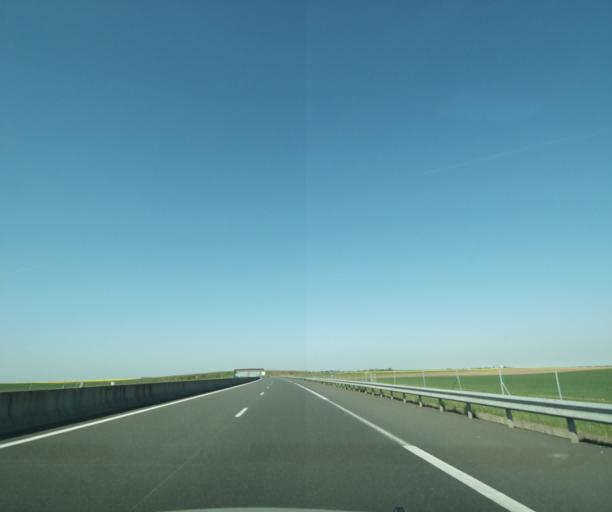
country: FR
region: Centre
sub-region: Departement du Loiret
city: Chilleurs-aux-Bois
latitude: 48.1154
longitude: 2.1482
